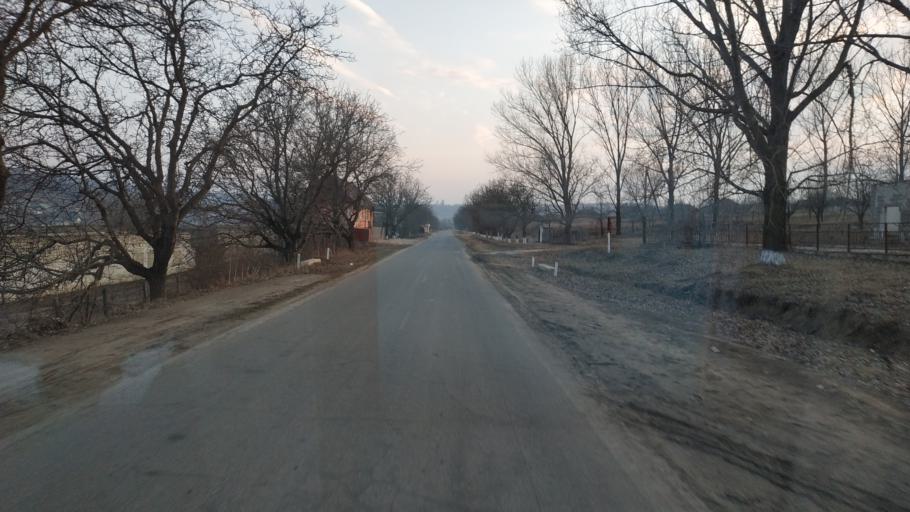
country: MD
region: Hincesti
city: Dancu
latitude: 46.6796
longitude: 28.3352
